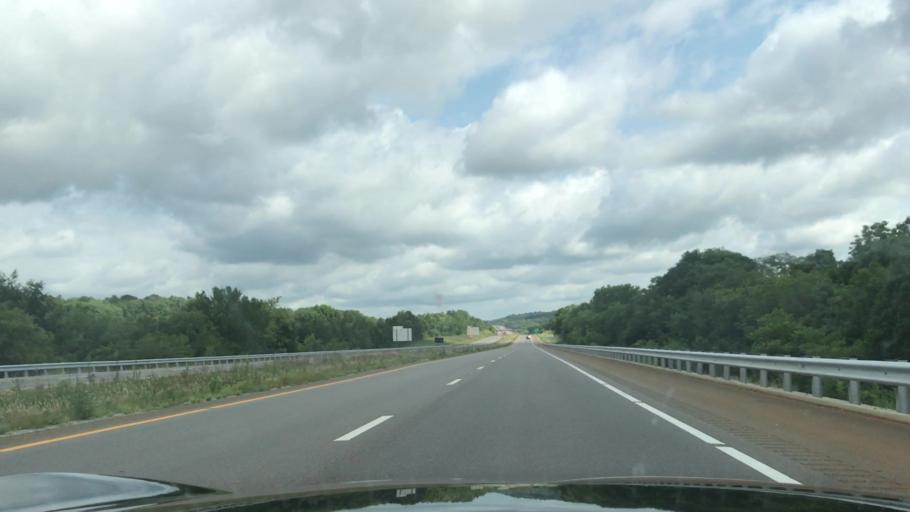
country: US
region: Kentucky
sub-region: Warren County
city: Bowling Green
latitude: 36.9765
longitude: -86.5006
